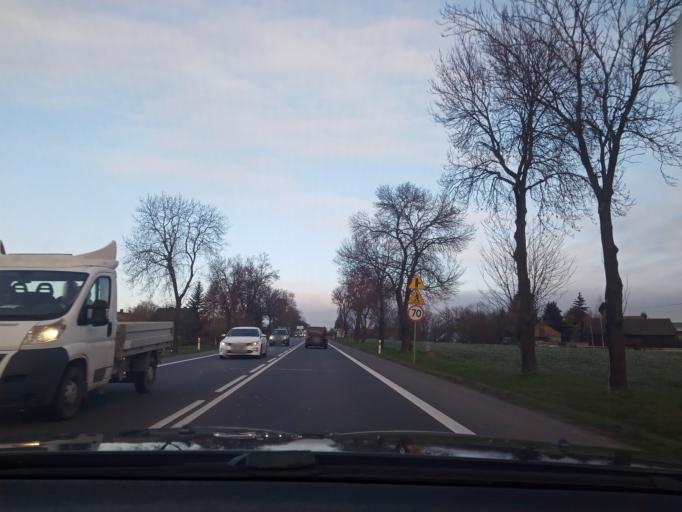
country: PL
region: Lesser Poland Voivodeship
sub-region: Powiat krakowski
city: Slomniki
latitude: 50.2632
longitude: 20.0777
